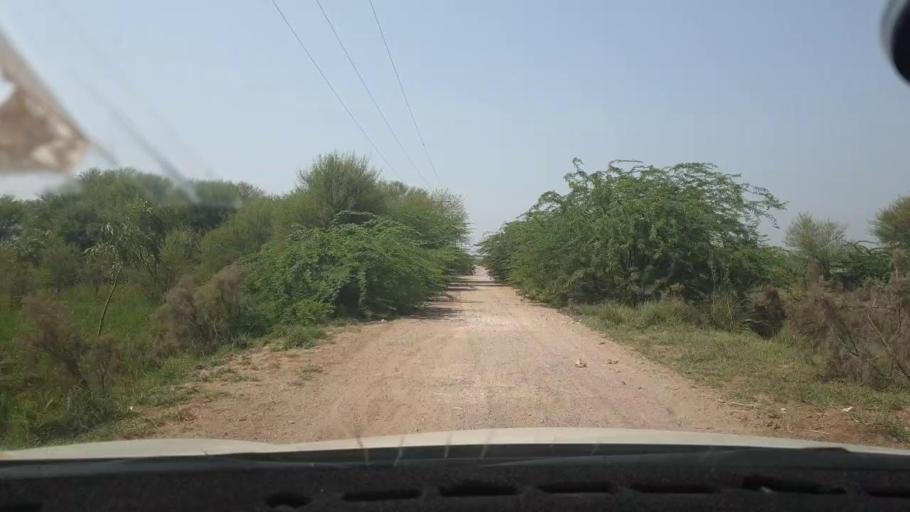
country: PK
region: Sindh
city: Tando Mittha Khan
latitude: 25.9210
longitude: 69.2501
